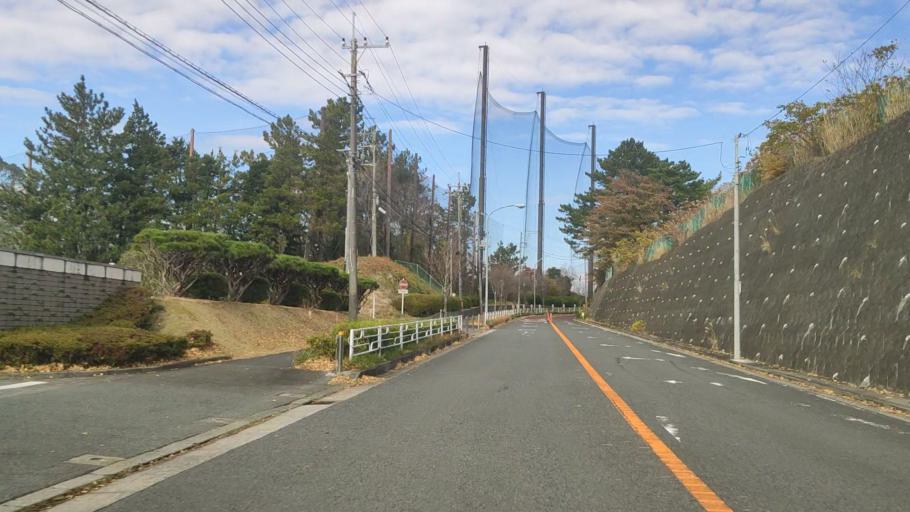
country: JP
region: Kanagawa
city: Minami-rinkan
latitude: 35.4443
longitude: 139.5385
